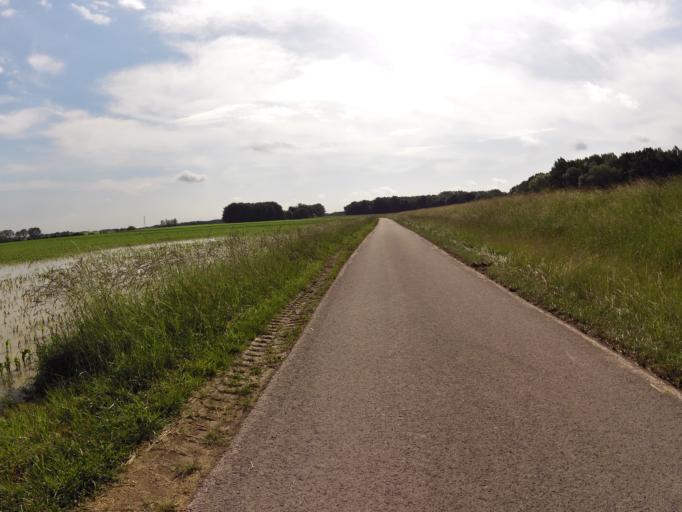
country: FR
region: Champagne-Ardenne
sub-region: Departement de l'Aube
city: Verrieres
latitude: 48.2723
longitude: 4.1489
